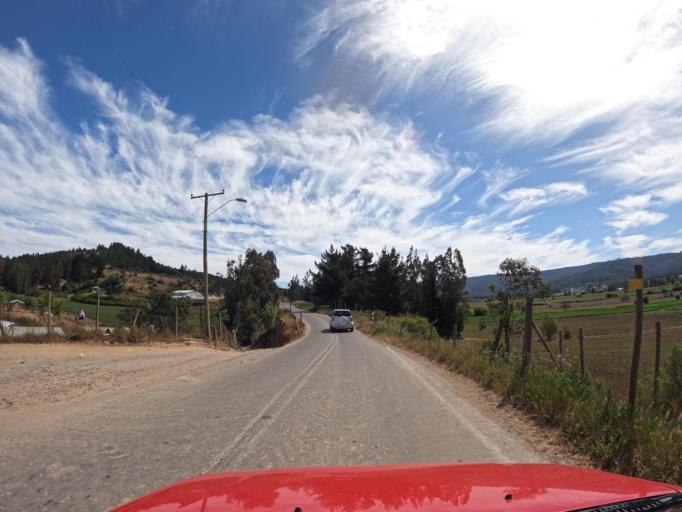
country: CL
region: Maule
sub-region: Provincia de Talca
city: Constitucion
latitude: -34.9923
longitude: -72.0054
